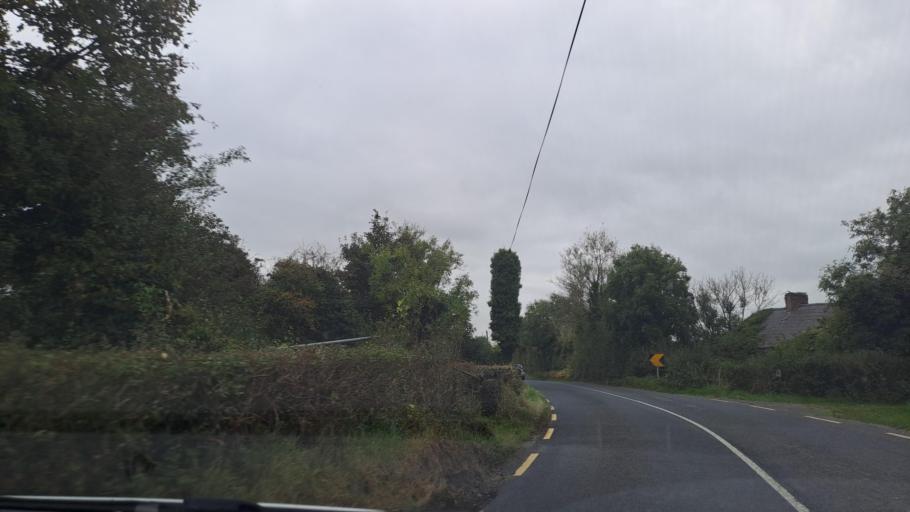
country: IE
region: Ulster
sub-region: An Cabhan
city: Cootehill
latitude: 54.0306
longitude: -7.0439
